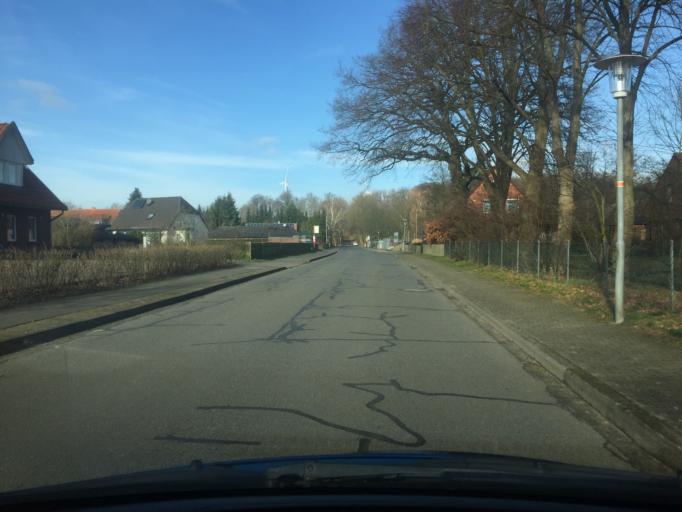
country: DE
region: Lower Saxony
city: Melbeck
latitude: 53.1796
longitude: 10.4017
